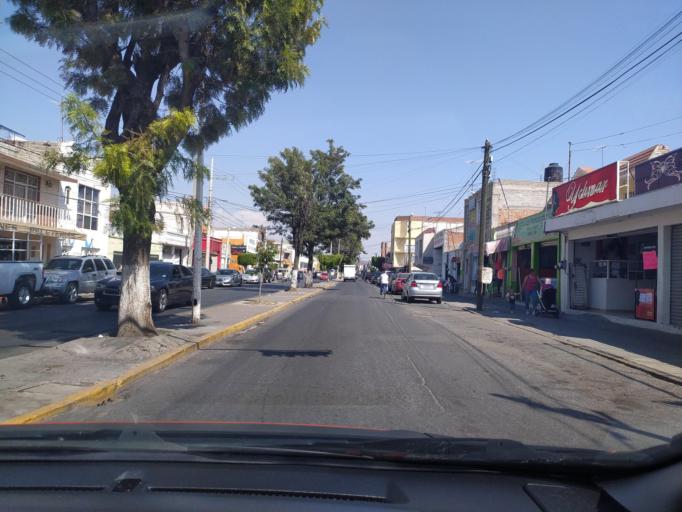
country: MX
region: Guanajuato
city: San Francisco del Rincon
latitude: 21.0159
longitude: -101.8550
